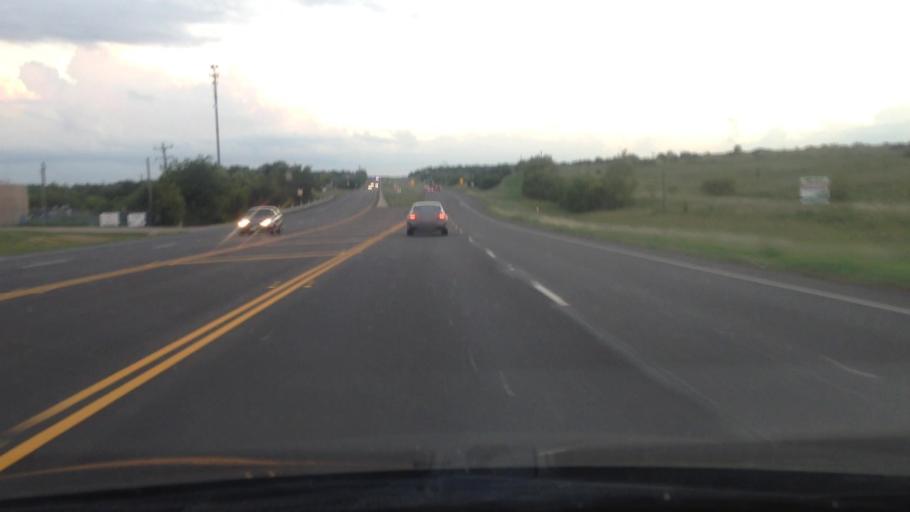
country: US
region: Texas
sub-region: Hood County
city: DeCordova
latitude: 32.5258
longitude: -97.6234
